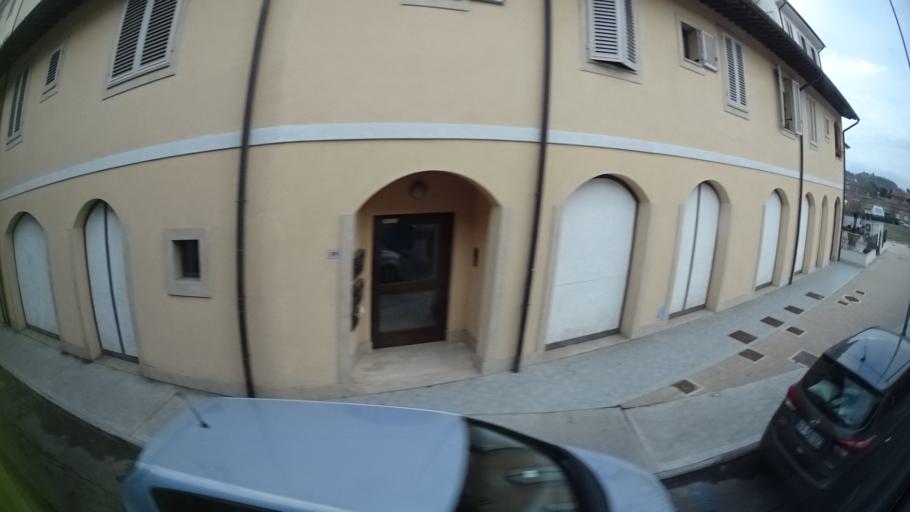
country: IT
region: Tuscany
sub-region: Provincia di Siena
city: Poggibonsi
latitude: 43.4665
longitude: 11.1497
